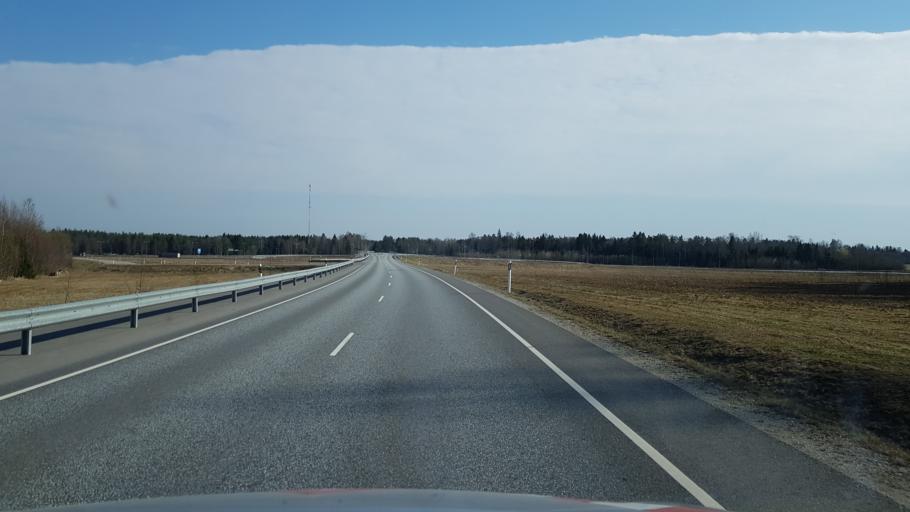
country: EE
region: Laeaene-Virumaa
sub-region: Kadrina vald
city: Kadrina
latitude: 59.4670
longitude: 25.9990
